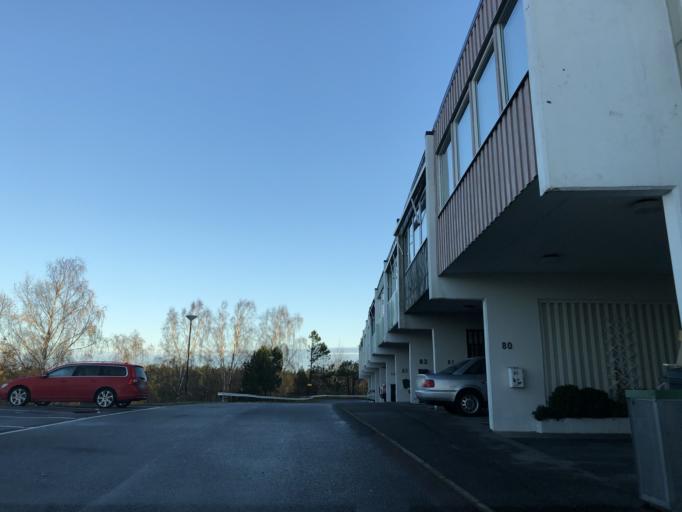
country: SE
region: Vaestra Goetaland
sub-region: Goteborg
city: Hammarkullen
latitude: 57.7782
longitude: 12.0262
